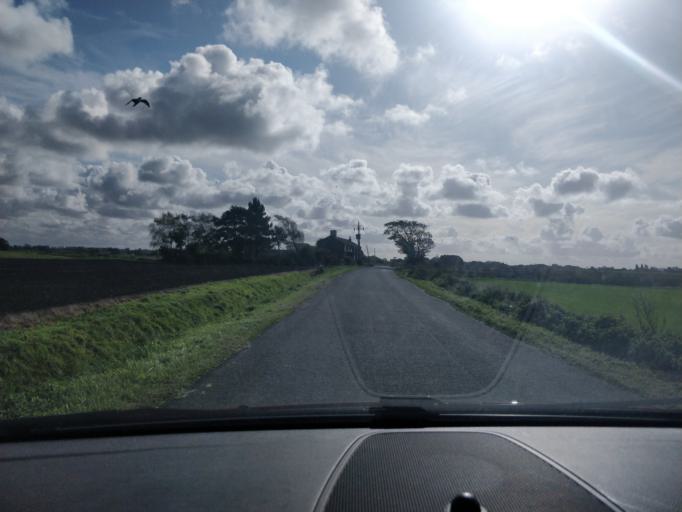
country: GB
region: England
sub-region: Lancashire
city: Banks
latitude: 53.6293
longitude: -2.9419
